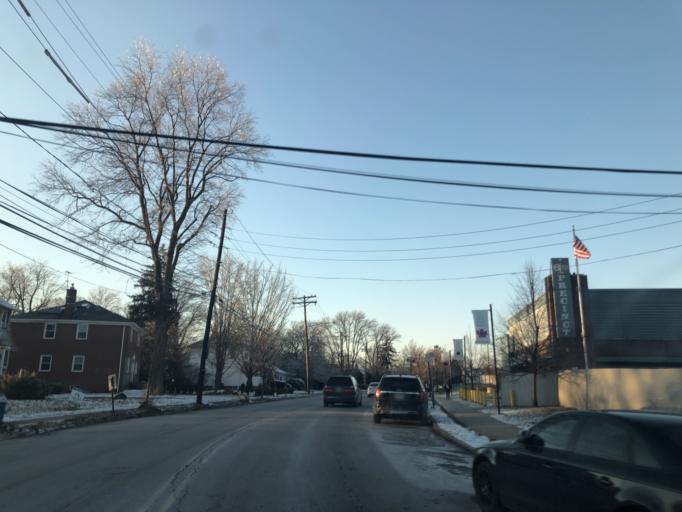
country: US
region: New Jersey
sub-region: Essex County
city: Irvington
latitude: 40.7348
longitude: -74.2496
